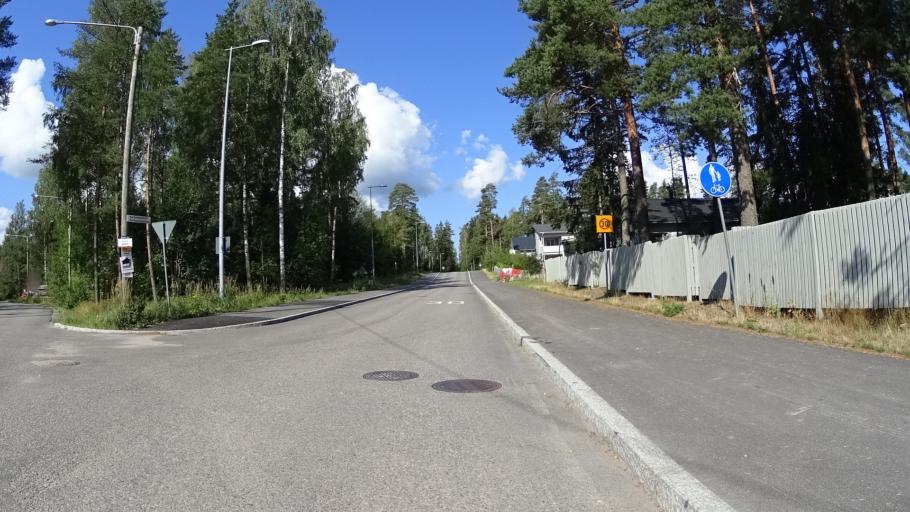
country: FI
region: Uusimaa
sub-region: Helsinki
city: Espoo
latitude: 60.1783
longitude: 24.6000
